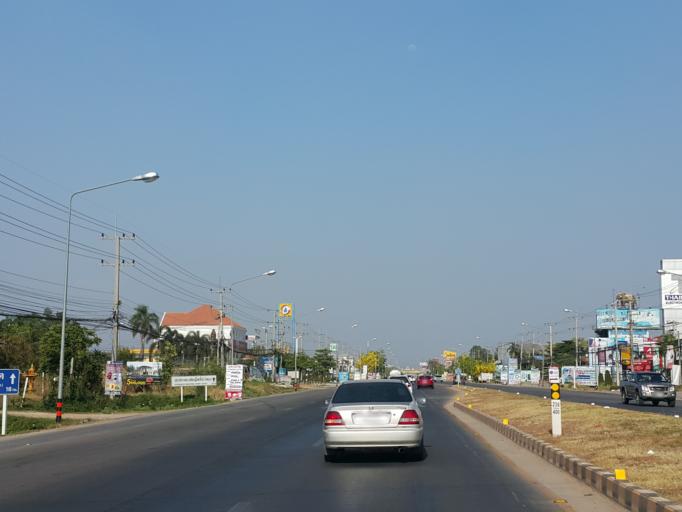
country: TH
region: Phitsanulok
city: Phitsanulok
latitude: 16.8163
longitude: 100.3057
